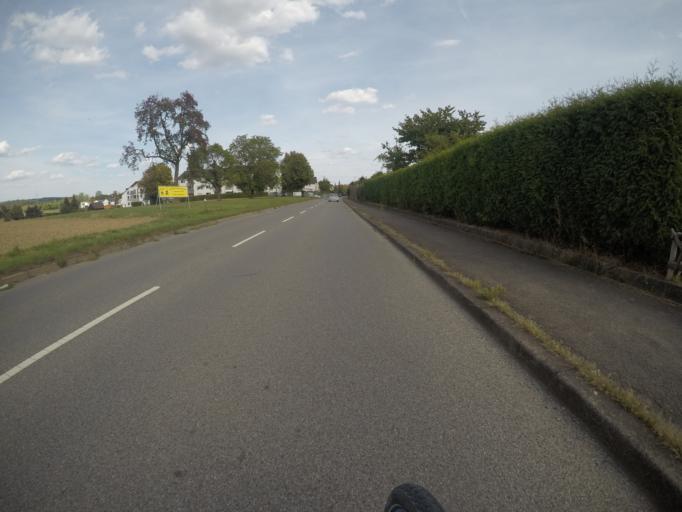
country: DE
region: Baden-Wuerttemberg
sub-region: Regierungsbezirk Stuttgart
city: Gartringen
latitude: 48.6423
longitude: 8.8896
